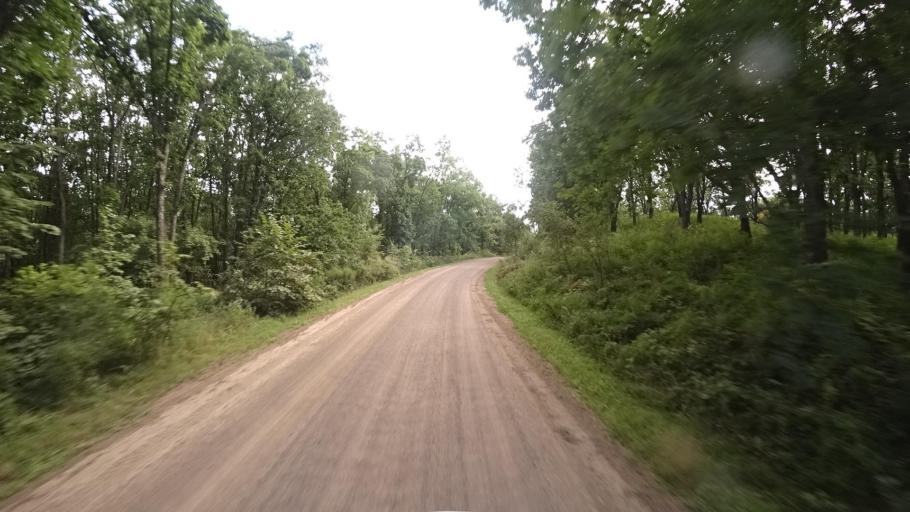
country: RU
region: Primorskiy
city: Dostoyevka
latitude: 44.3504
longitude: 133.5195
